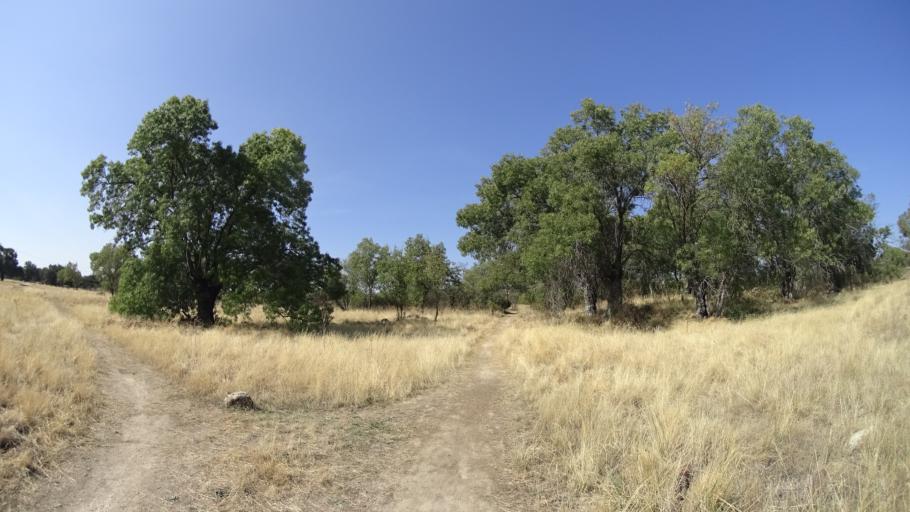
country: ES
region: Madrid
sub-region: Provincia de Madrid
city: Galapagar
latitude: 40.5846
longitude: -3.9833
